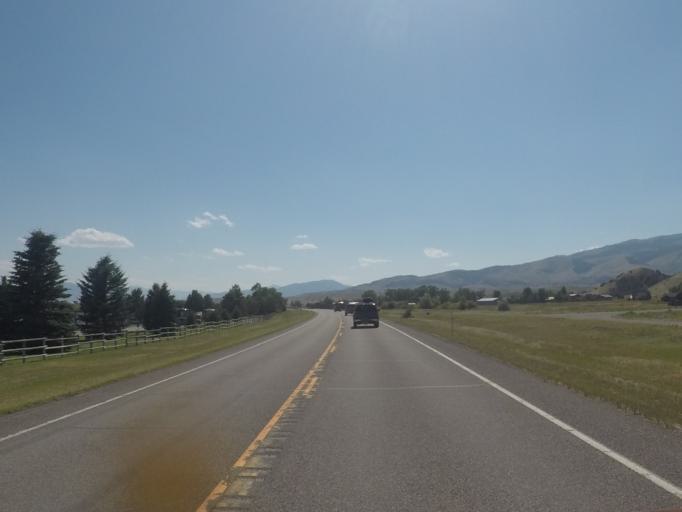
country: US
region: Montana
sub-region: Park County
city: Livingston
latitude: 45.4167
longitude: -110.6857
